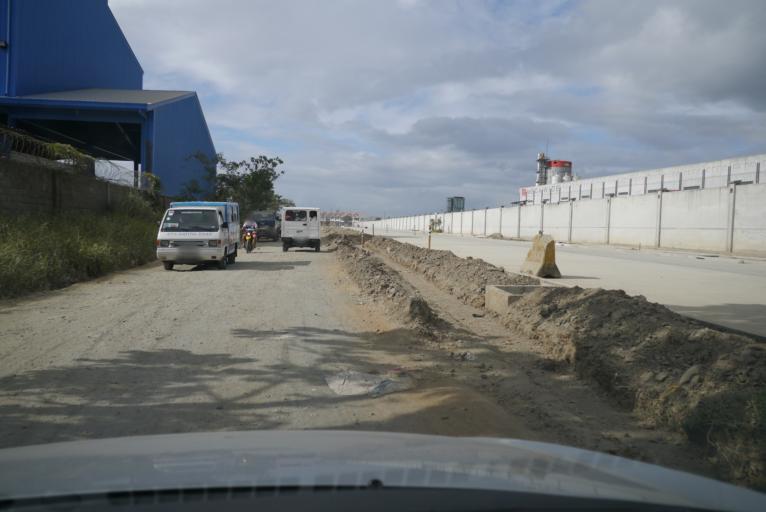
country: PH
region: Calabarzon
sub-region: Province of Rizal
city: Taytay
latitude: 14.5467
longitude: 121.1285
